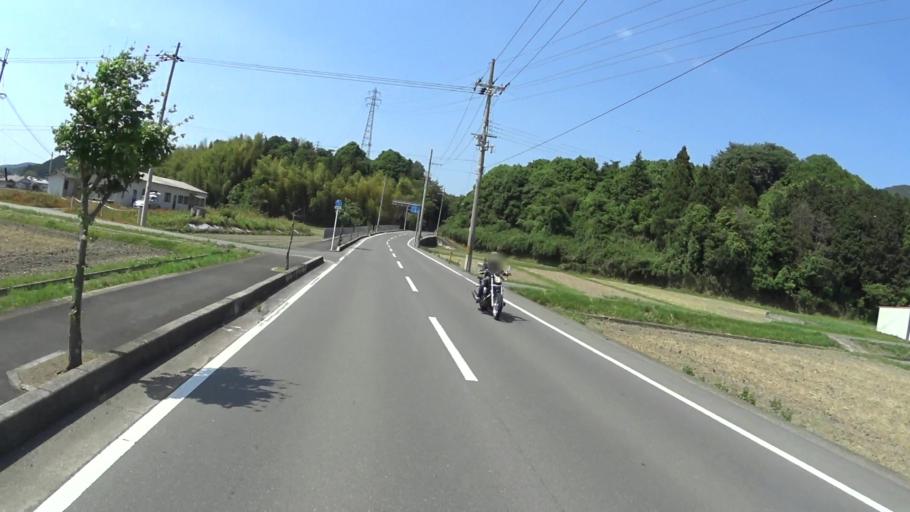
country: JP
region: Kyoto
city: Kameoka
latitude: 35.0622
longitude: 135.5672
